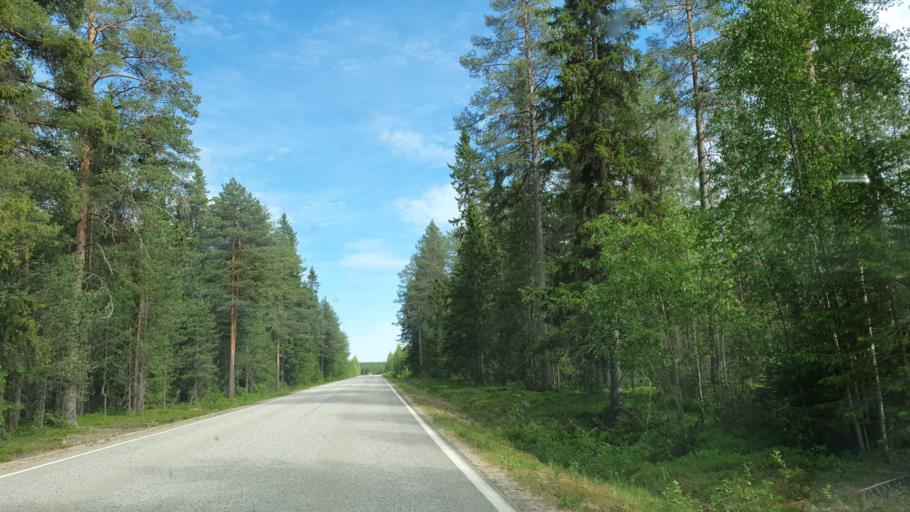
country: FI
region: Kainuu
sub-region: Kehys-Kainuu
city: Suomussalmi
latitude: 64.5740
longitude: 29.0093
